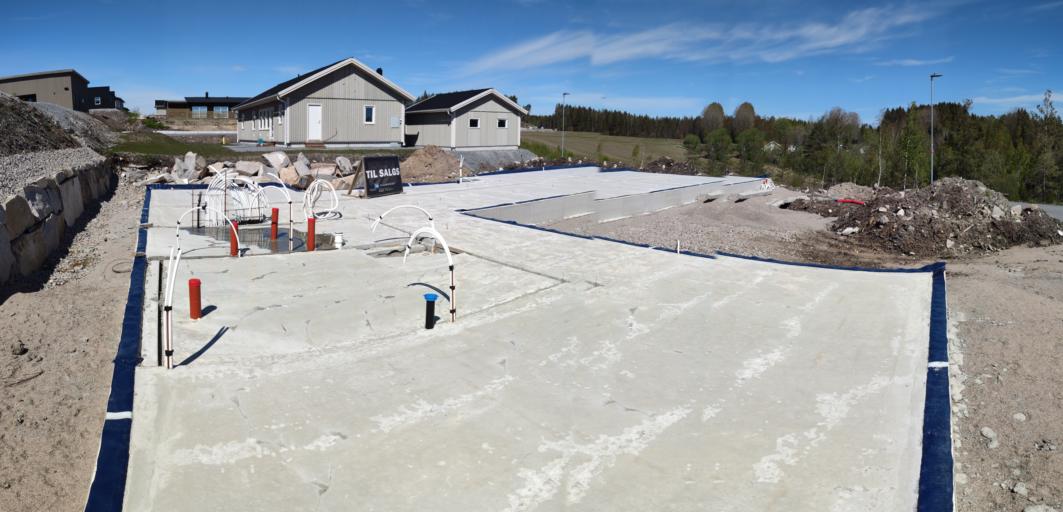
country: NO
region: Ostfold
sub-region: Halden
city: Halden
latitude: 59.1068
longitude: 11.4423
